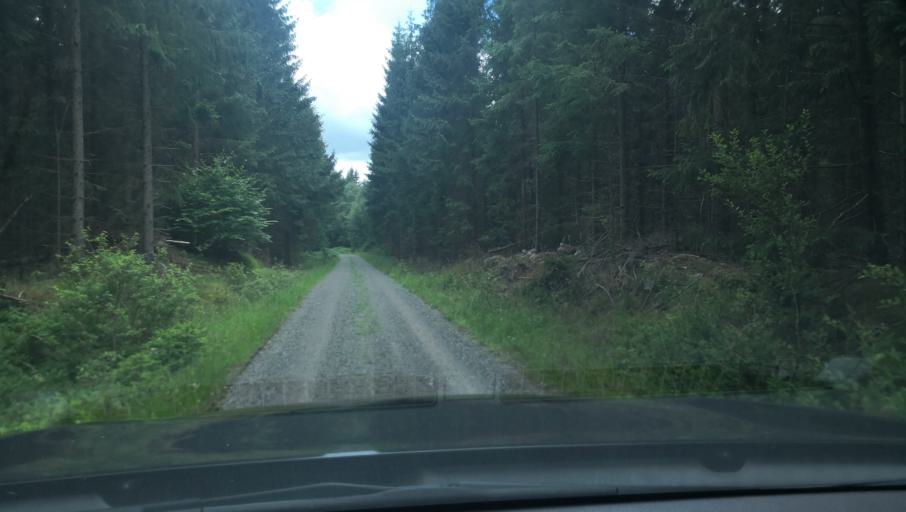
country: SE
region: Skane
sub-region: Simrishamns Kommun
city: Kivik
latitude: 55.6098
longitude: 14.1180
